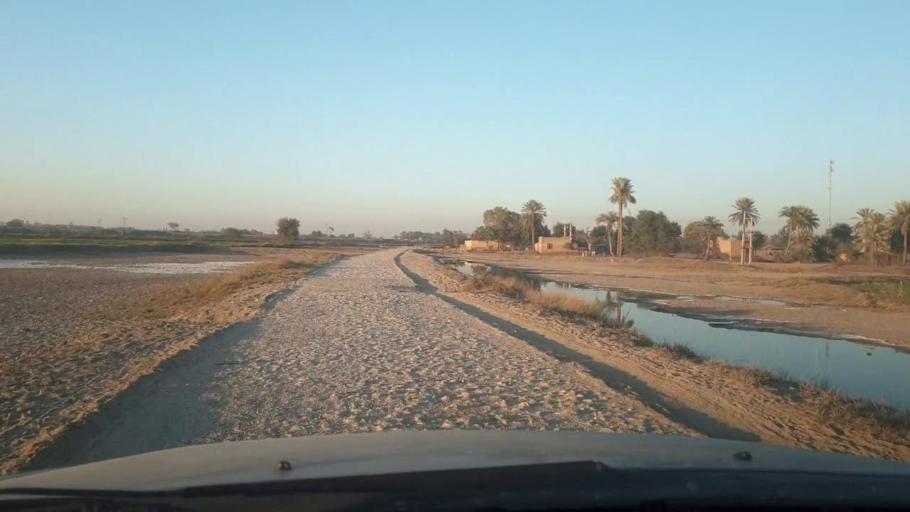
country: PK
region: Sindh
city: Pano Aqil
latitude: 27.9144
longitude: 69.1939
